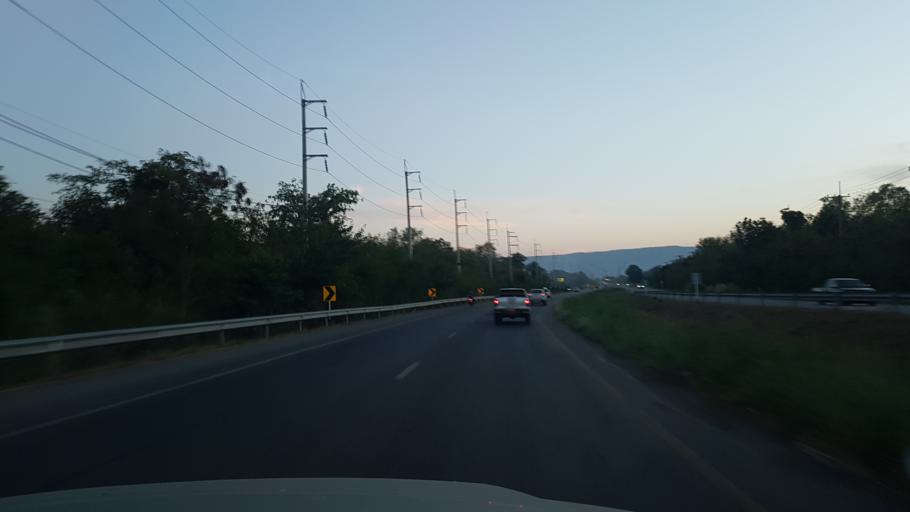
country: TH
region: Chaiyaphum
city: Phu Khiao
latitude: 16.4157
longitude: 102.1326
